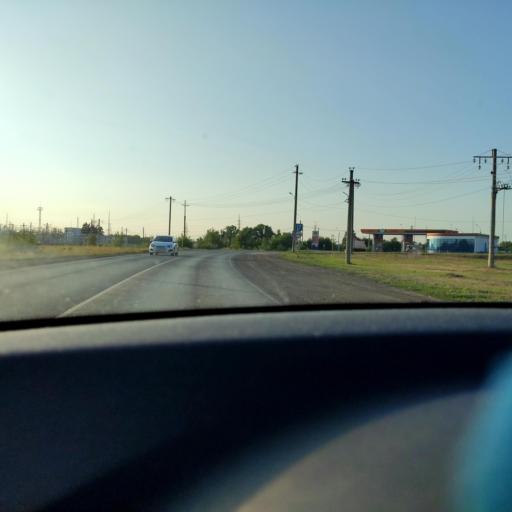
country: RU
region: Samara
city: Kinel'
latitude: 53.2373
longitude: 50.5808
